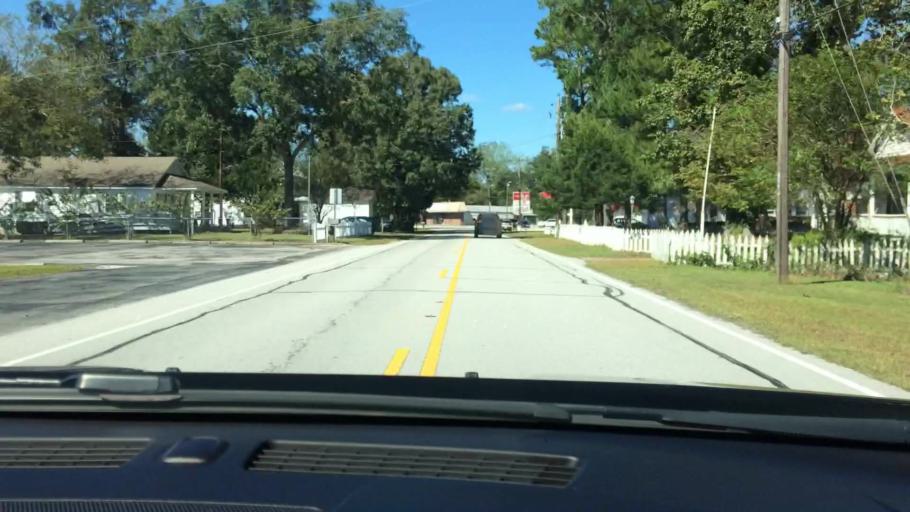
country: US
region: North Carolina
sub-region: Pitt County
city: Grifton
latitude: 35.2909
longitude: -77.3351
